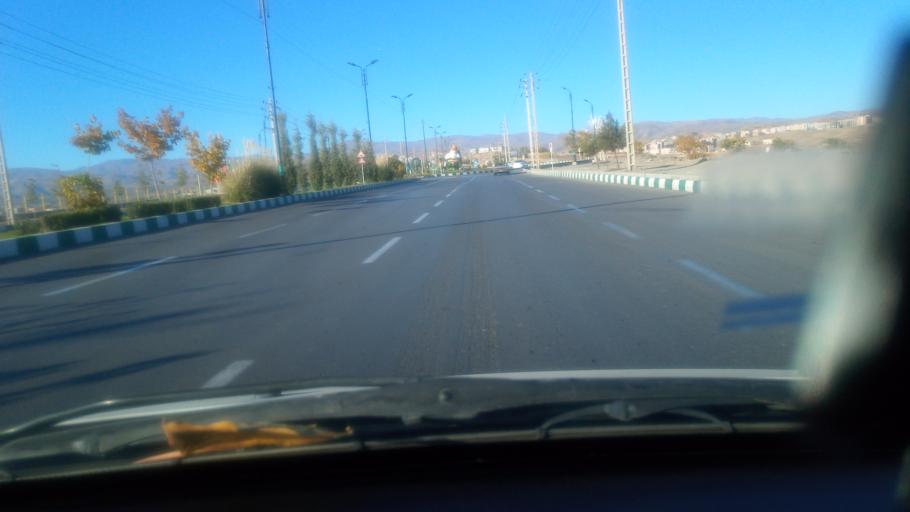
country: IR
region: Razavi Khorasan
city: Torqabeh
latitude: 36.3181
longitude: 59.3883
